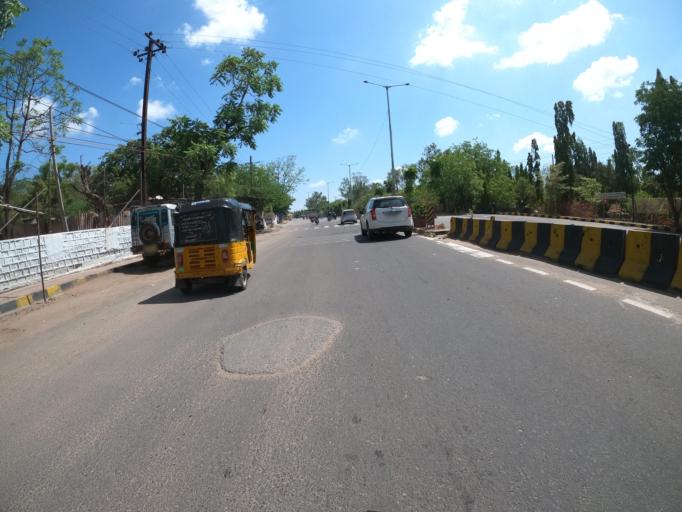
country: IN
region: Telangana
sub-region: Hyderabad
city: Hyderabad
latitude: 17.3825
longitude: 78.4222
